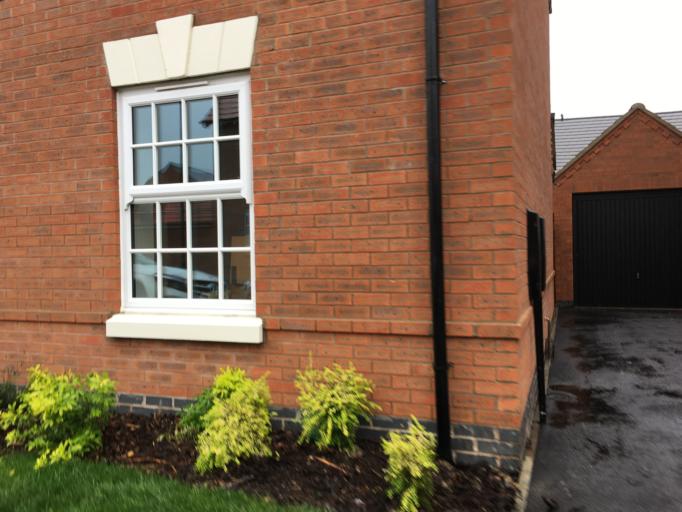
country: GB
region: England
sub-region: Warwickshire
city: Rugby
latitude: 52.3586
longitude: -1.1864
